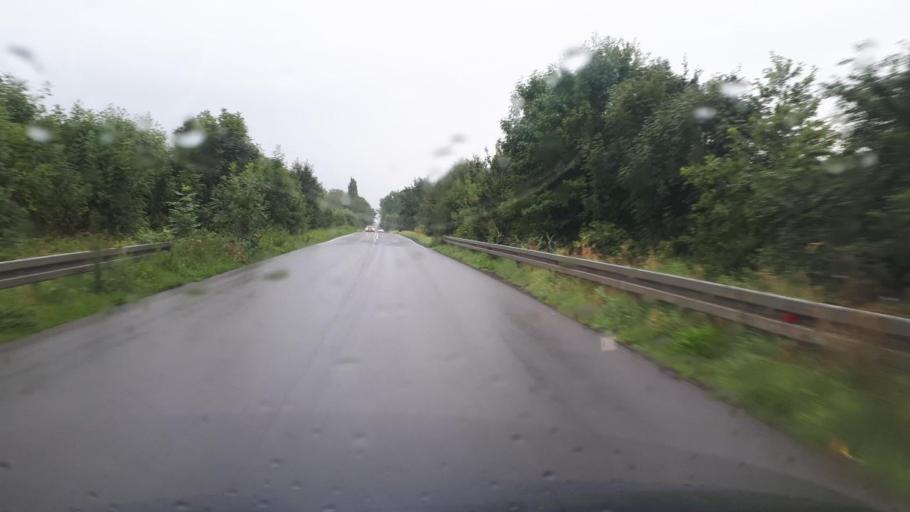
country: PL
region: Silesian Voivodeship
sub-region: Powiat tarnogorski
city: Wieszowa
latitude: 50.3451
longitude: 18.7156
